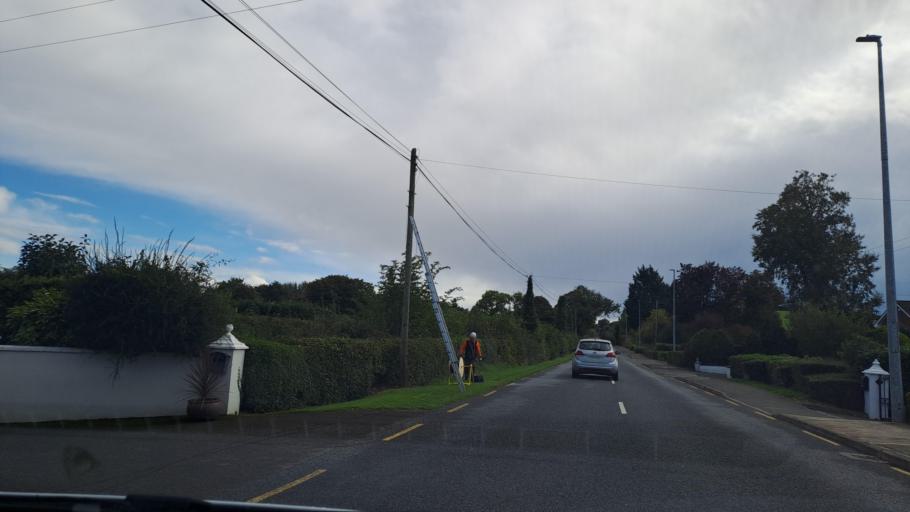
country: IE
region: Ulster
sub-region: County Monaghan
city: Carrickmacross
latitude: 53.9630
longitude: -6.7080
